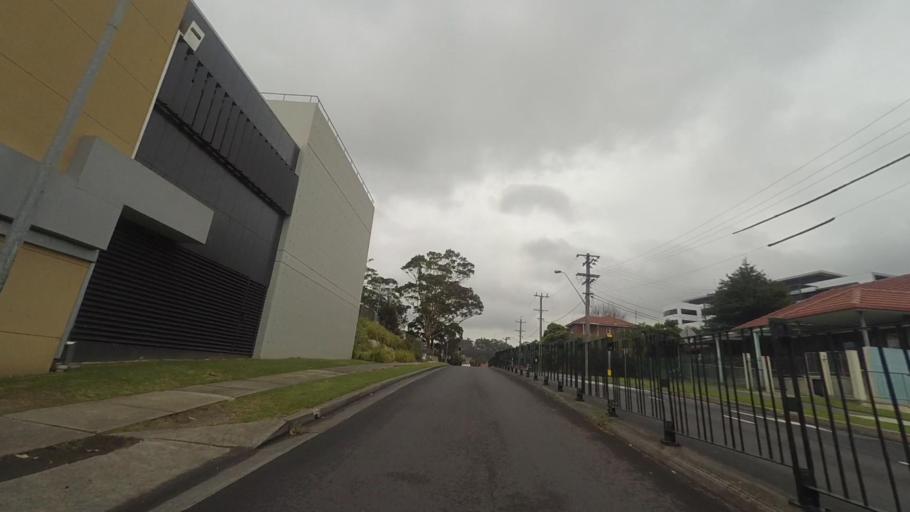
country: AU
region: New South Wales
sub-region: Wollongong
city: Gwynneville
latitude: -34.4248
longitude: 150.8824
